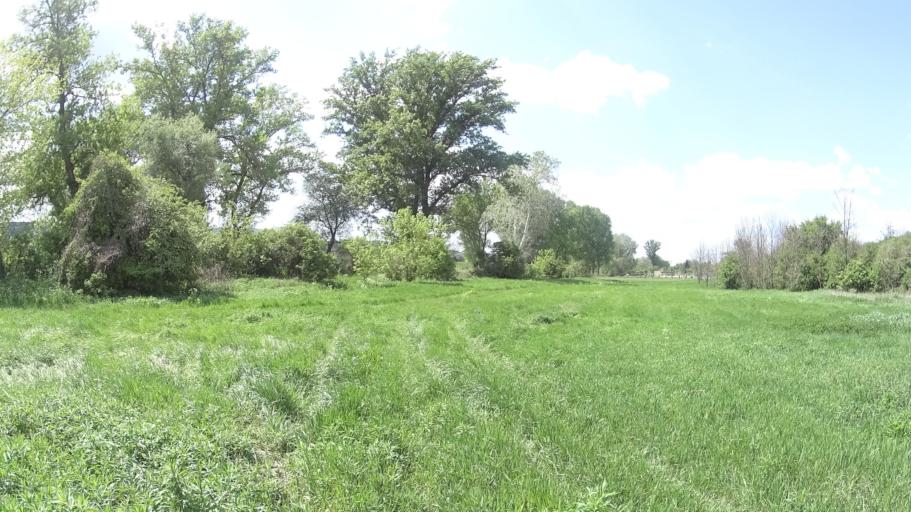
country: HU
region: Komarom-Esztergom
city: Dorog
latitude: 47.7159
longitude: 18.7544
